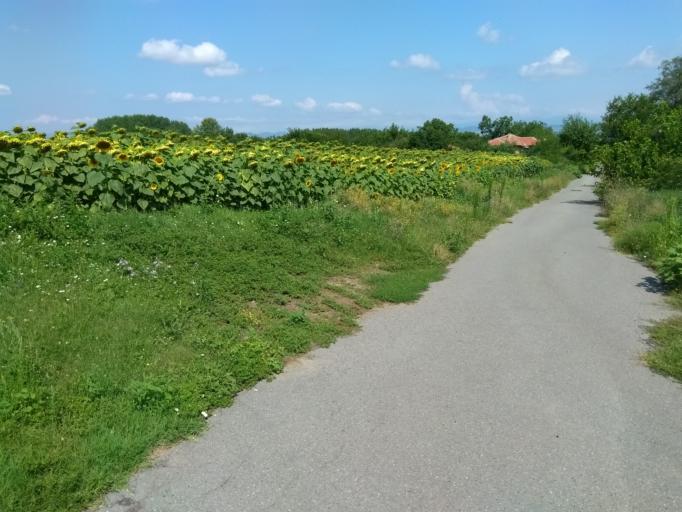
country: BG
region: Sliven
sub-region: Obshtina Sliven
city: Kermen
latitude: 42.4558
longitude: 26.1380
